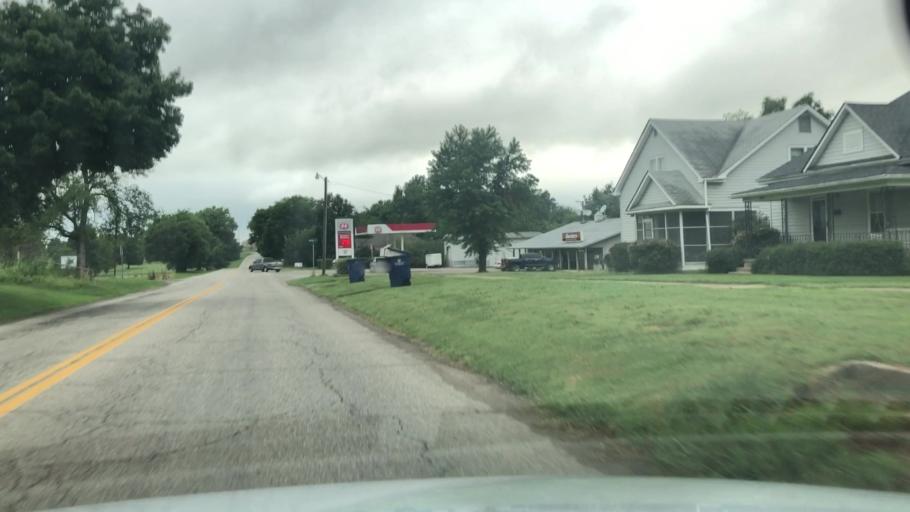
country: US
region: Oklahoma
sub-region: Nowata County
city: Nowata
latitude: 36.7027
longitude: -95.6422
